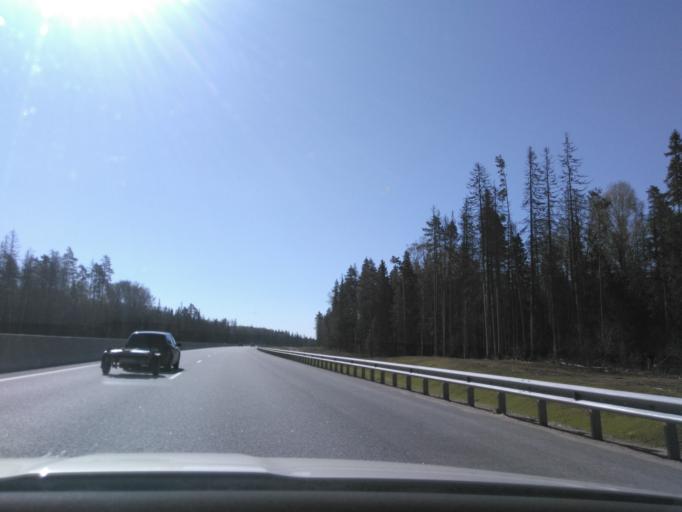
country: RU
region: Moskovskaya
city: Mendeleyevo
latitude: 56.0543
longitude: 37.2539
